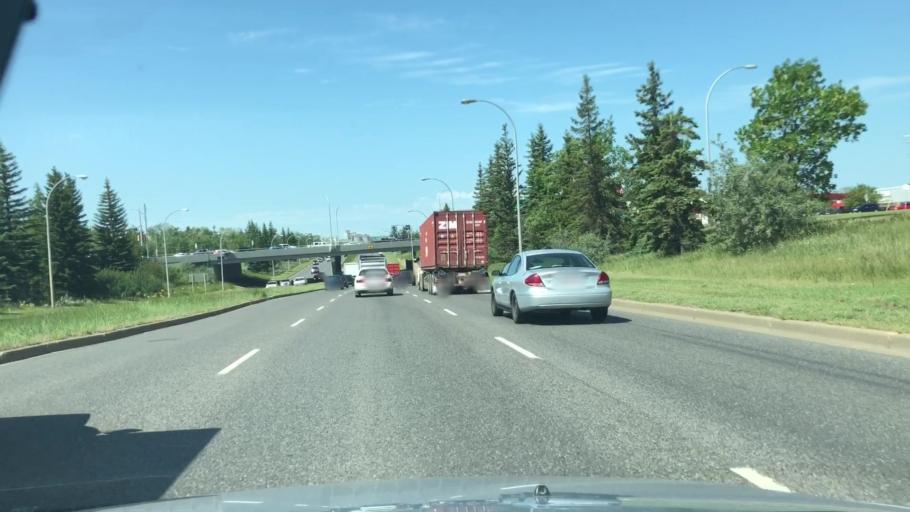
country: CA
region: Alberta
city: Edmonton
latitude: 53.5812
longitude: -113.5541
